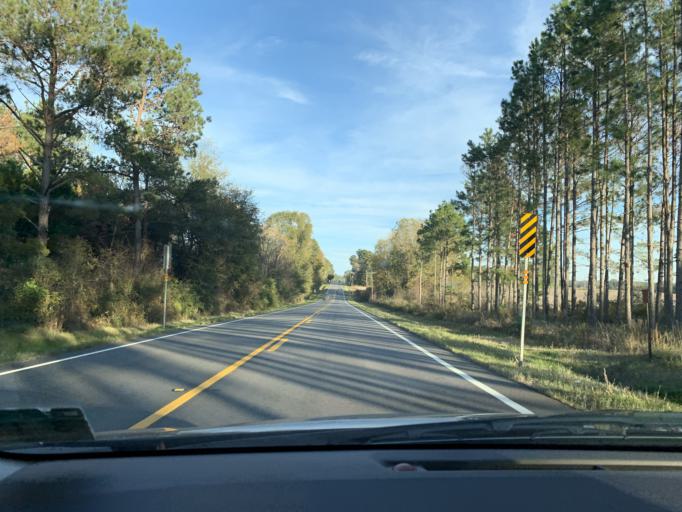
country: US
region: Georgia
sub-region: Irwin County
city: Ocilla
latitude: 31.5956
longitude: -83.1354
